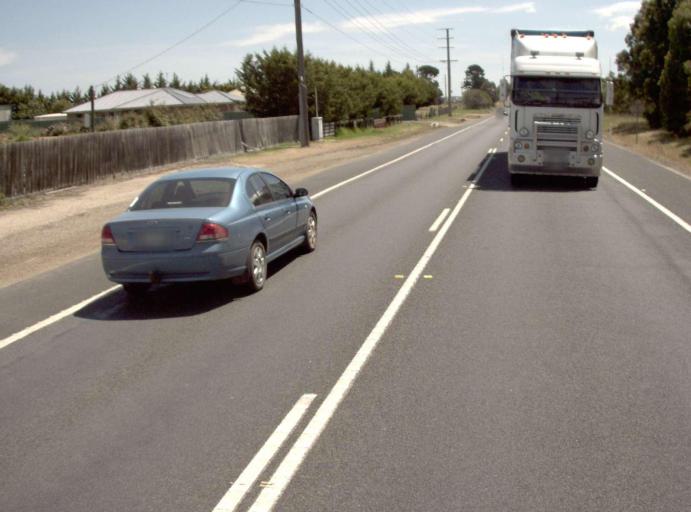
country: AU
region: Victoria
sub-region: Wellington
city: Sale
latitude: -38.1054
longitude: 146.9121
